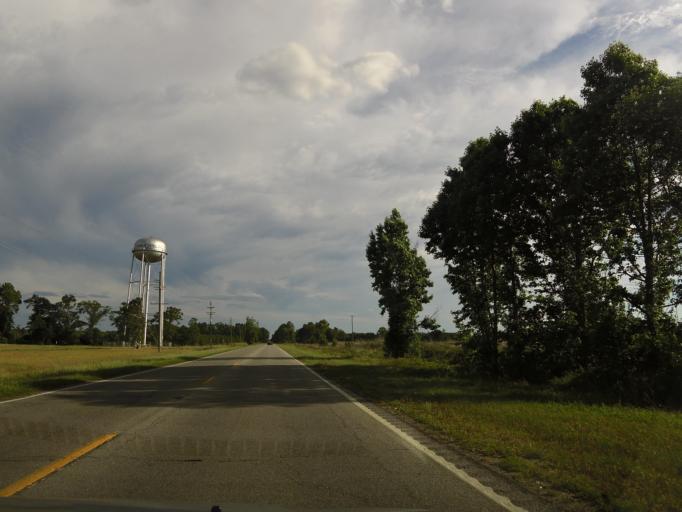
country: US
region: South Carolina
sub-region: Hampton County
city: Estill
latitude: 32.7804
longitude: -81.2408
